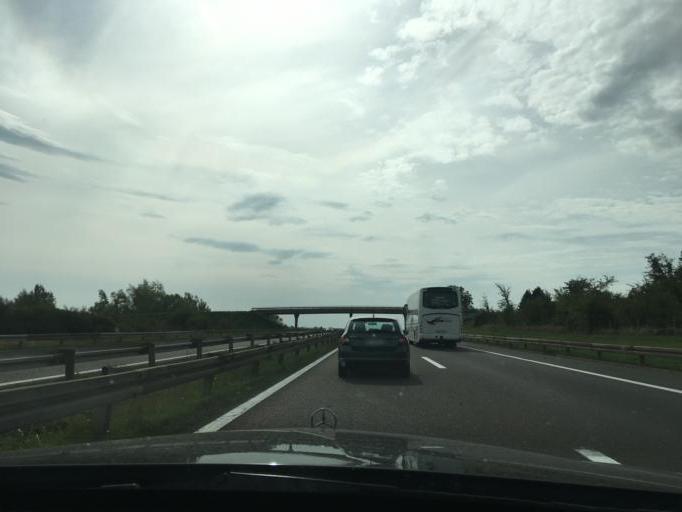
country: RS
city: Lugavcina
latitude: 44.4456
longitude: 21.0468
